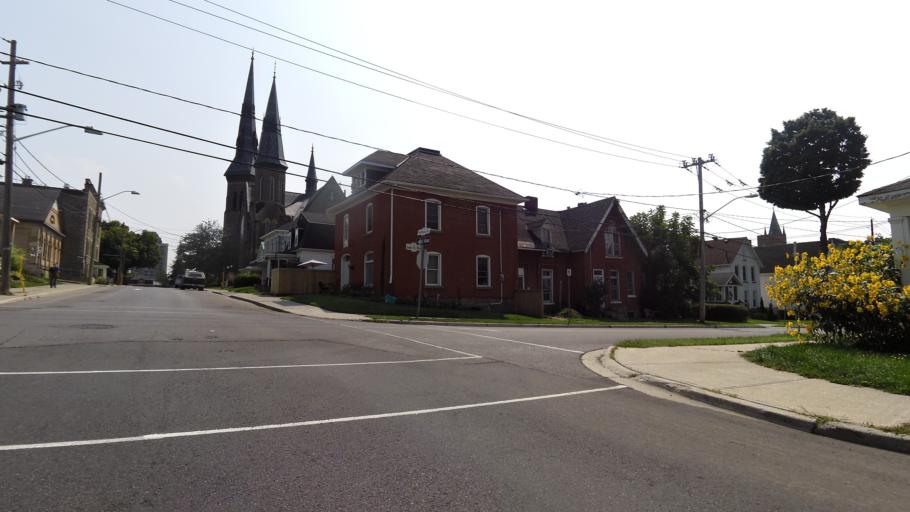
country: CA
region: Ontario
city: Brockville
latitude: 44.5913
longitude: -75.6871
